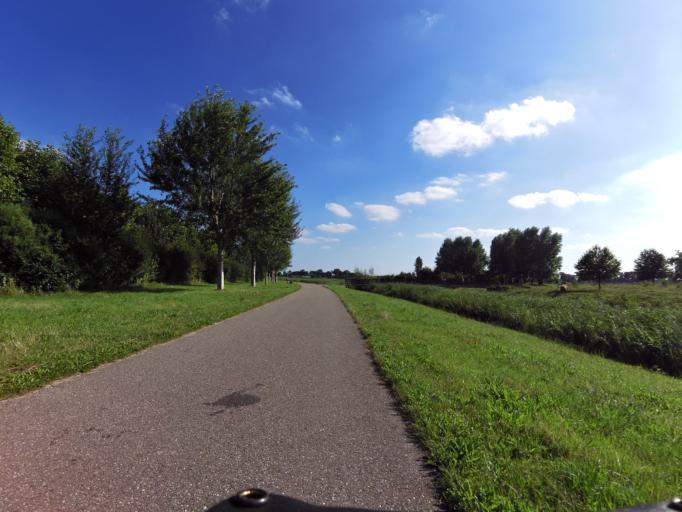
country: NL
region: South Holland
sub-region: Gemeente Binnenmaas
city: Heinenoord
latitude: 51.8536
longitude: 4.4702
